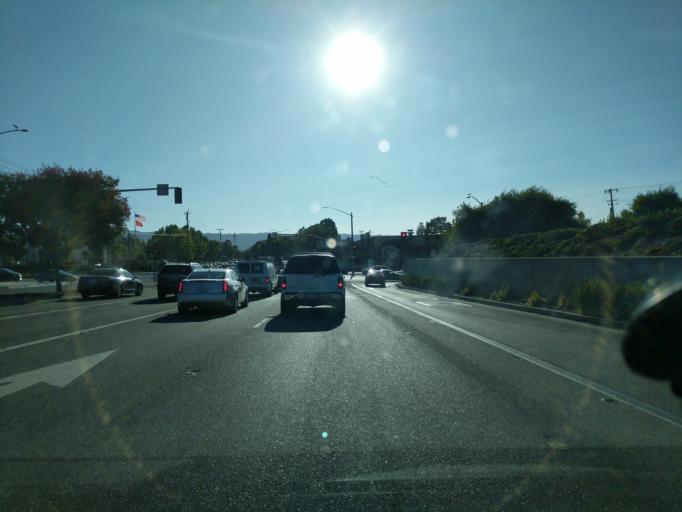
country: US
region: California
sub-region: Alameda County
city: Pleasanton
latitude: 37.6705
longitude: -121.8571
